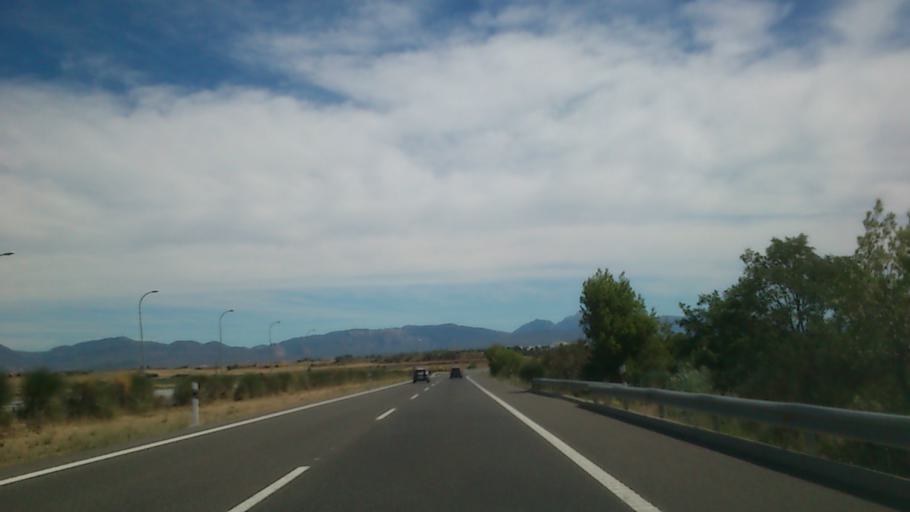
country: ES
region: Aragon
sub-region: Provincia de Huesca
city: Alerre
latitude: 42.0928
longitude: -0.4767
